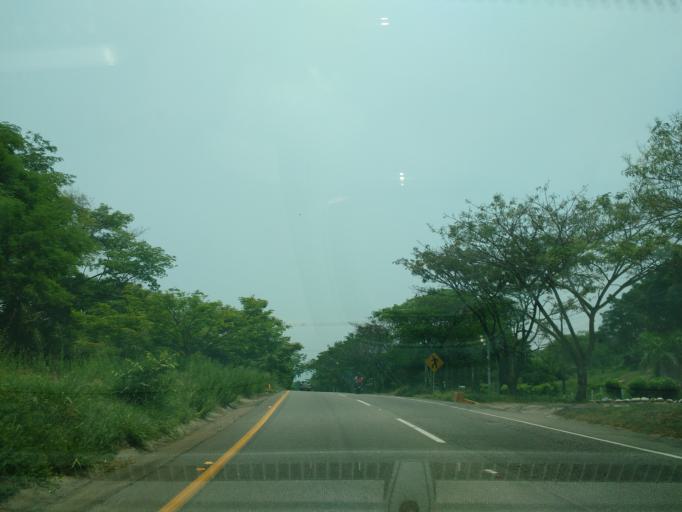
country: CO
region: Tolima
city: Melgar
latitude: 4.2156
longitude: -74.6693
